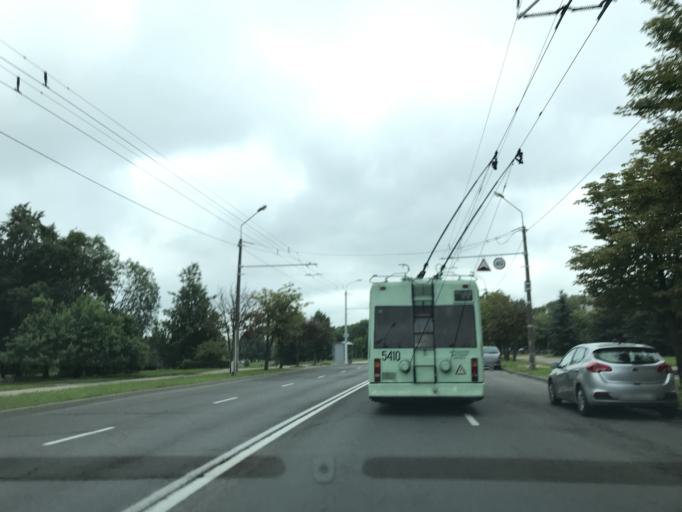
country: BY
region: Minsk
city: Borovlyany
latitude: 53.9487
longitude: 27.6411
